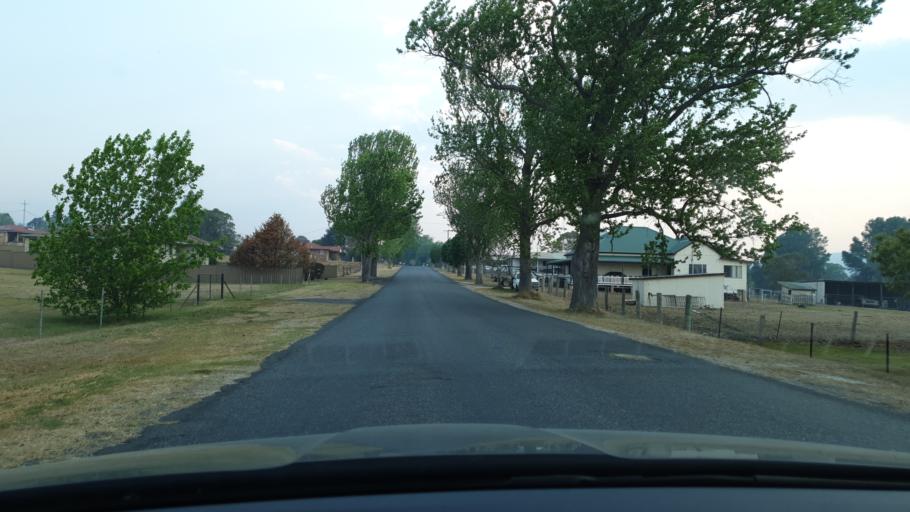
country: AU
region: New South Wales
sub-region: Tenterfield Municipality
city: Carrolls Creek
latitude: -29.0429
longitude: 152.0234
